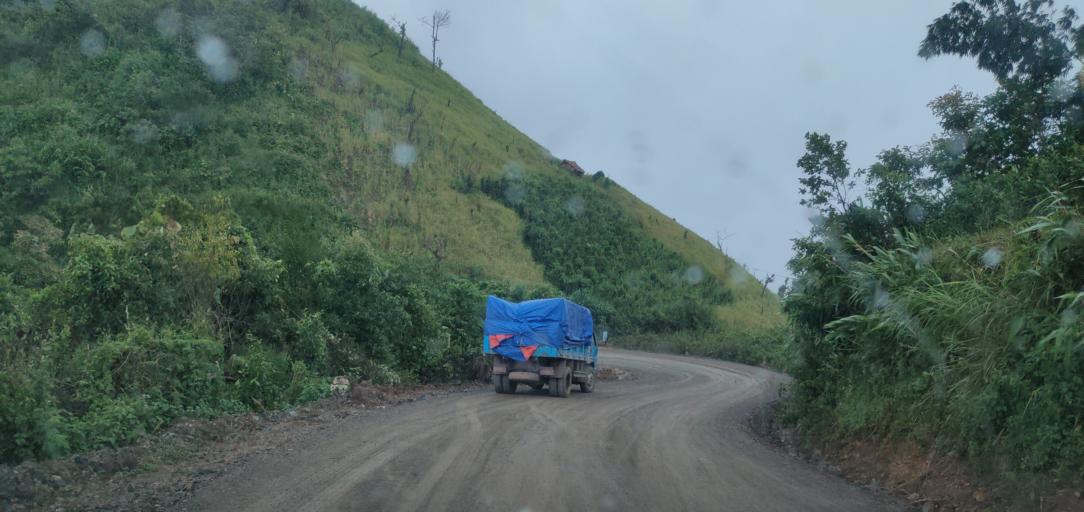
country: LA
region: Phongsali
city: Phongsali
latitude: 21.4304
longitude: 102.1605
